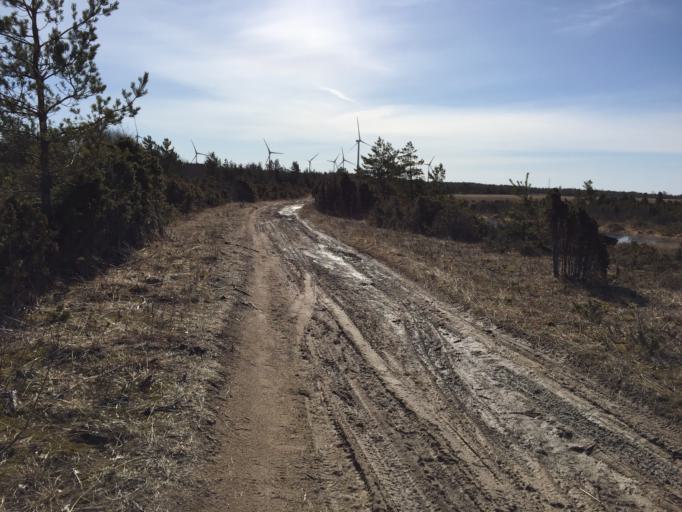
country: EE
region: Laeaene
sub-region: Haapsalu linn
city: Haapsalu
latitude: 58.6493
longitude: 23.5085
